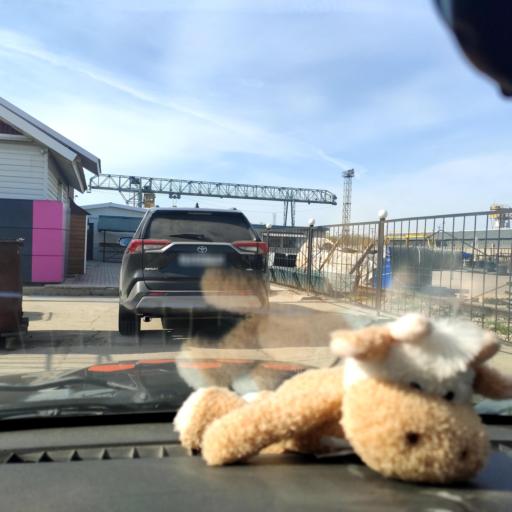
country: RU
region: Samara
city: Tol'yatti
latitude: 53.5734
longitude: 49.2751
